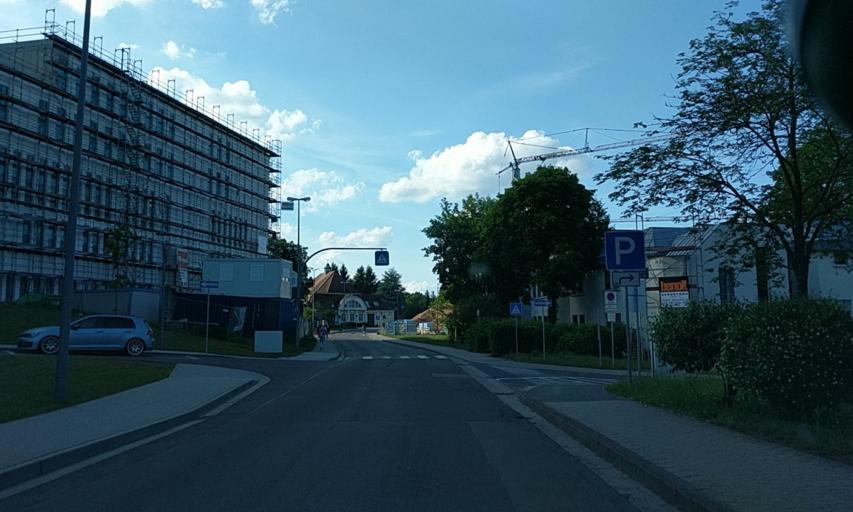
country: DE
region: Saarland
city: Homburg
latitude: 49.3065
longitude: 7.3461
